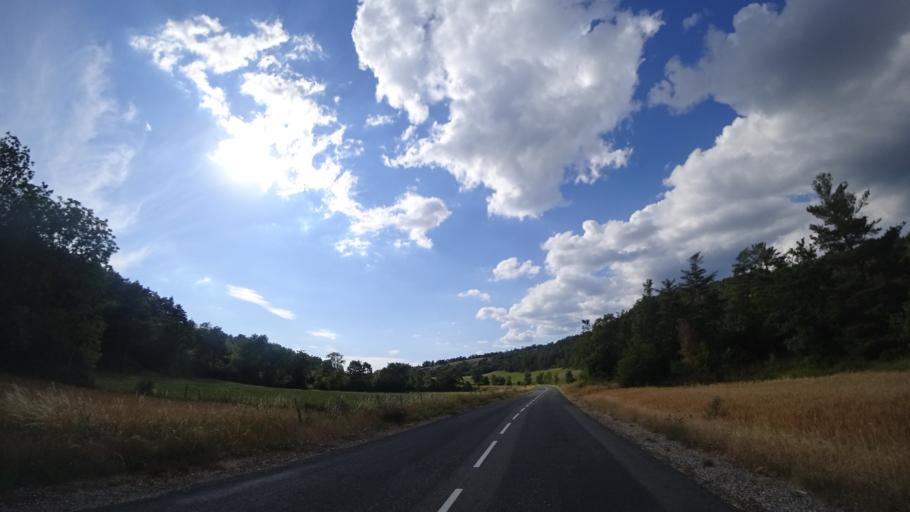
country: FR
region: Languedoc-Roussillon
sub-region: Departement de la Lozere
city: Chanac
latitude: 44.3743
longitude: 3.3324
